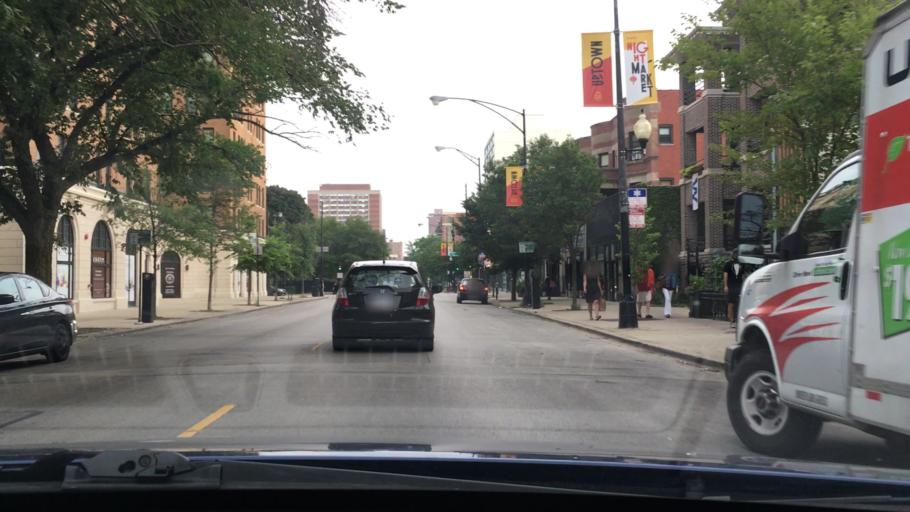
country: US
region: Illinois
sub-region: Cook County
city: Evanston
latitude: 41.9742
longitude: -87.6550
